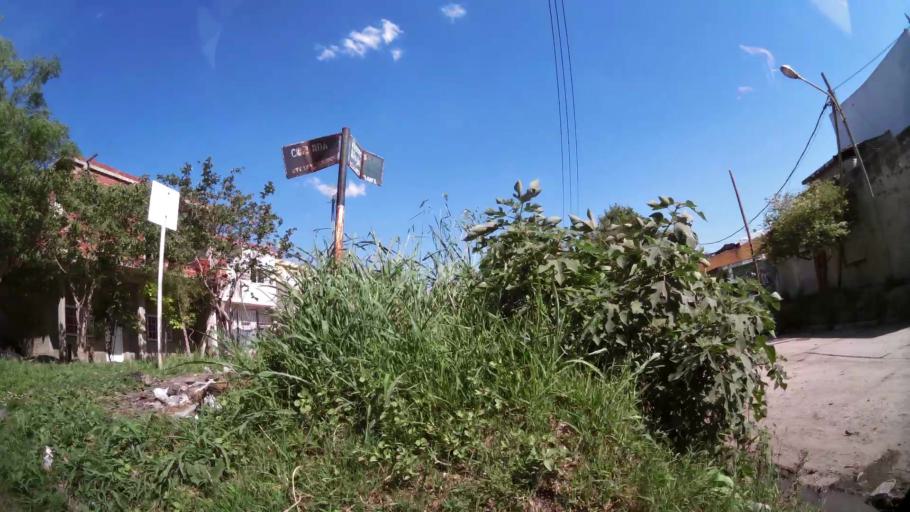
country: AR
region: Buenos Aires F.D.
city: Villa Lugano
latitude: -34.7047
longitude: -58.4718
